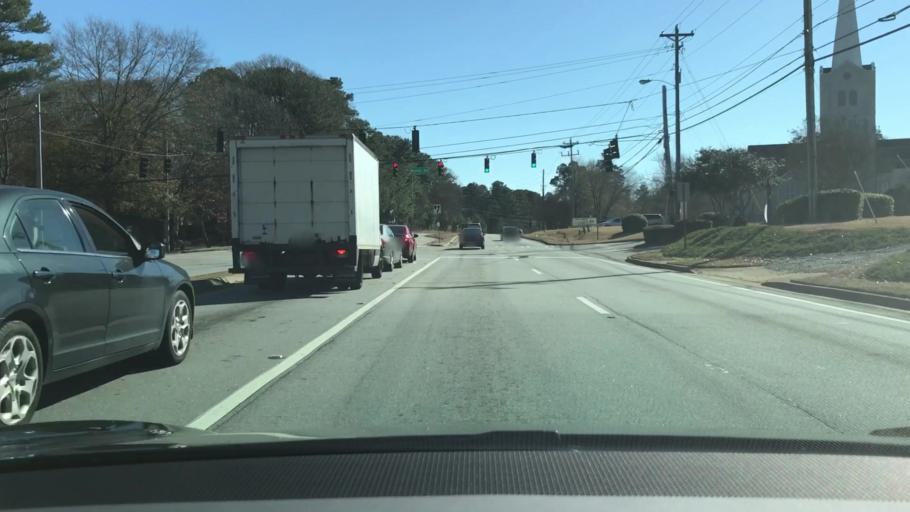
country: US
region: Georgia
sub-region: Gwinnett County
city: Lawrenceville
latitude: 33.9893
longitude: -84.0286
